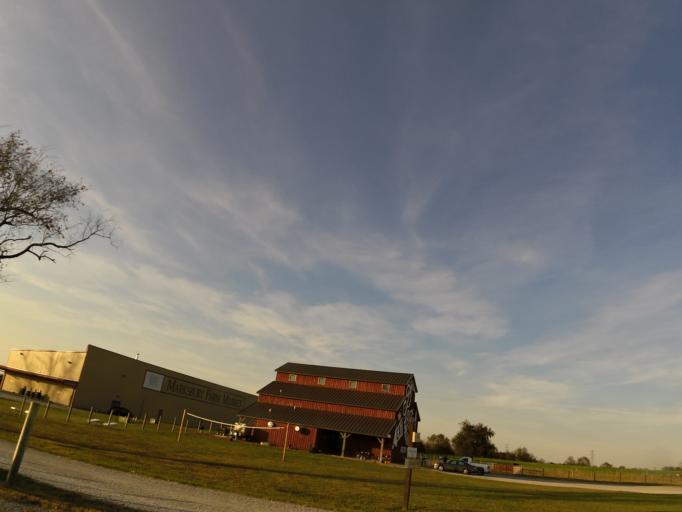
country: US
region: Kentucky
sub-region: Boyle County
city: Danville
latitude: 37.6992
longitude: -84.6665
